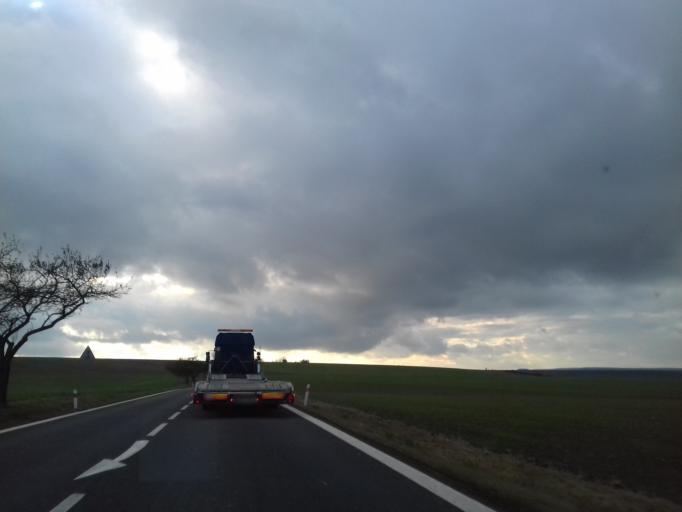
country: CZ
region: Pardubicky
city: Pomezi
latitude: 49.7275
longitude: 16.3226
